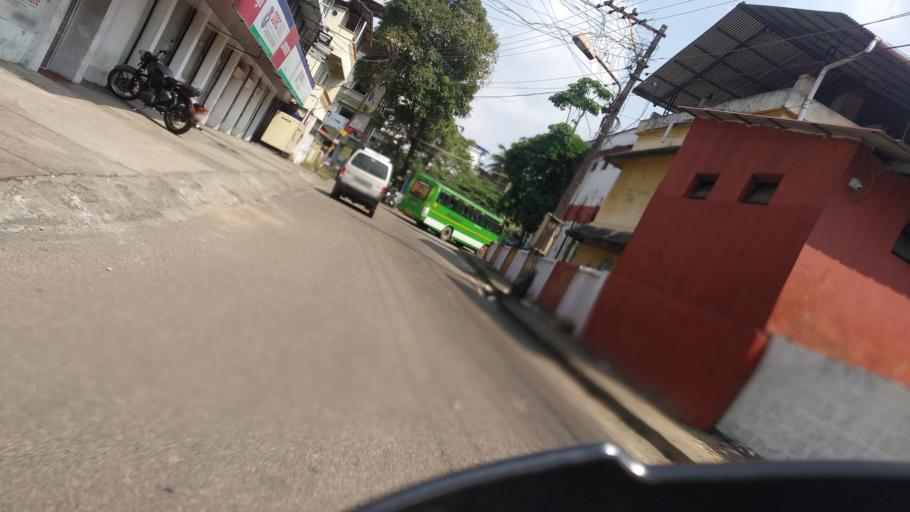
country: IN
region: Kerala
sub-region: Ernakulam
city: Cochin
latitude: 9.9725
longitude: 76.2815
